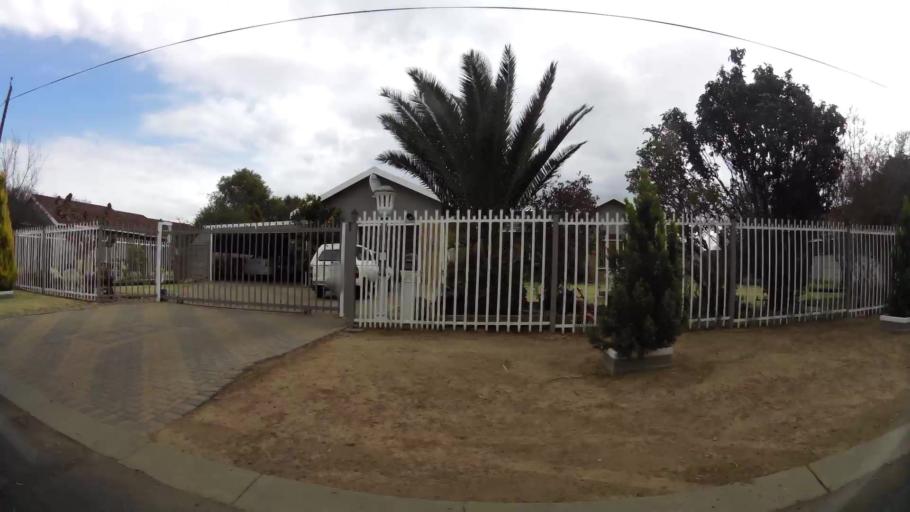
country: ZA
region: Orange Free State
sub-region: Fezile Dabi District Municipality
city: Kroonstad
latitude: -27.6289
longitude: 27.2405
